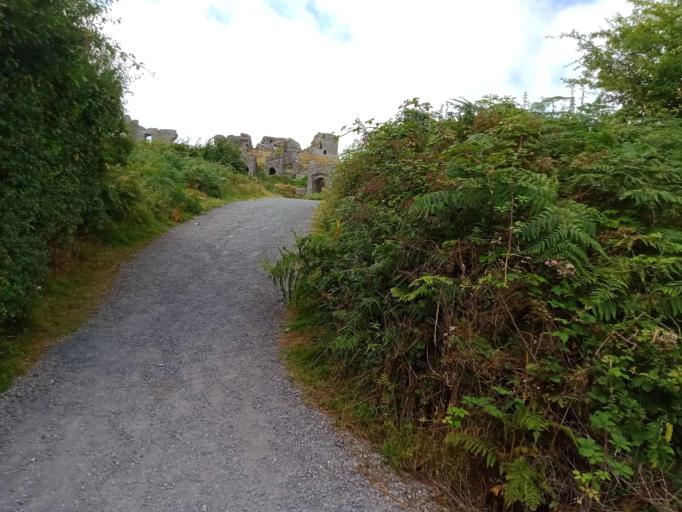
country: IE
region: Leinster
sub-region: Laois
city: Stradbally
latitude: 53.0311
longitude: -7.2086
